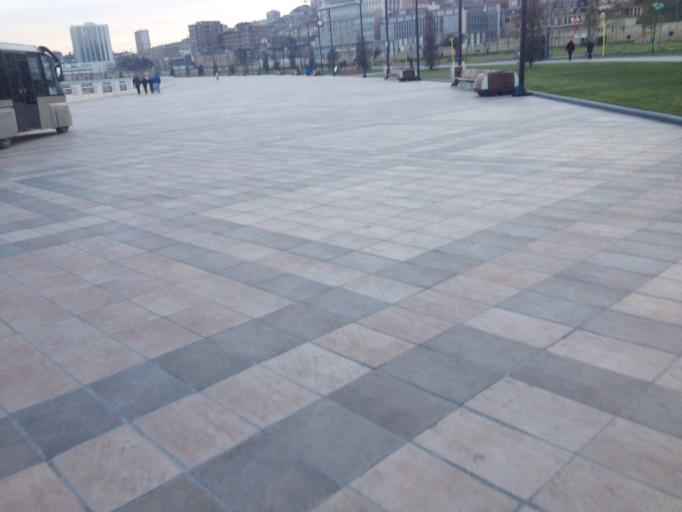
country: AZ
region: Baki
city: Badamdar
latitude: 40.3530
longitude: 49.8369
